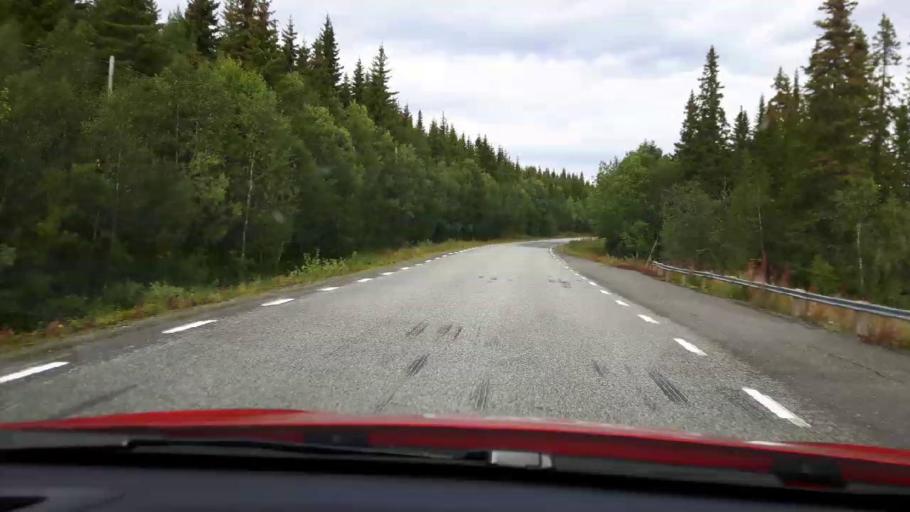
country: SE
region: Jaemtland
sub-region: Are Kommun
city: Are
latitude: 63.7209
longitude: 12.9681
